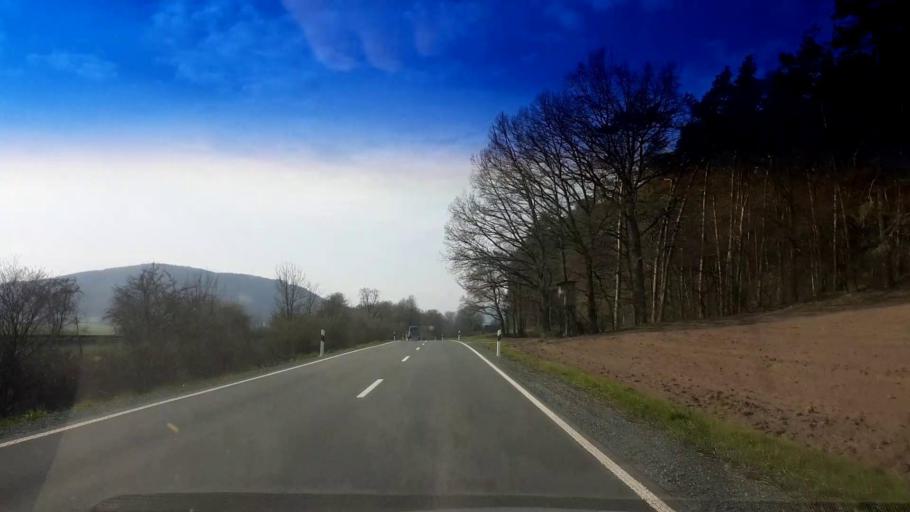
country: DE
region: Bavaria
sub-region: Upper Franconia
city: Harsdorf
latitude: 50.0346
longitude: 11.5551
